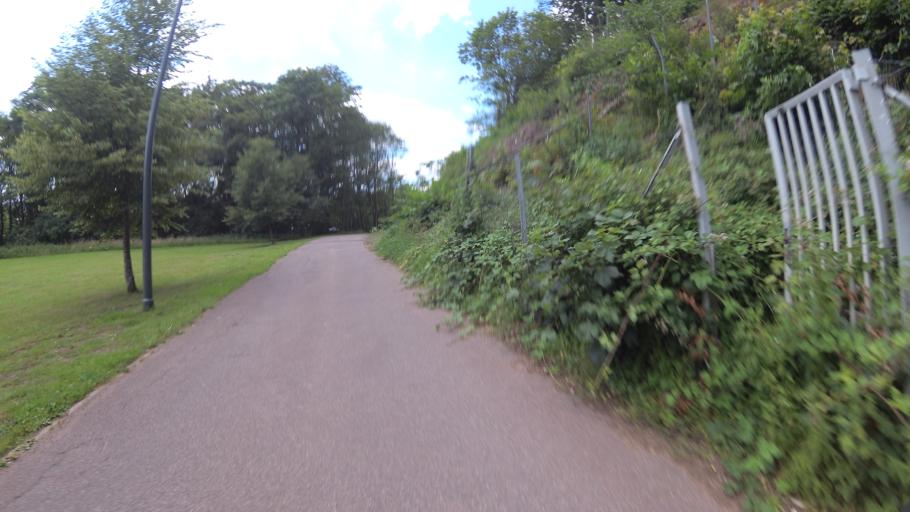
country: DE
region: Saarland
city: Wadern
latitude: 49.5292
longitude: 6.8978
